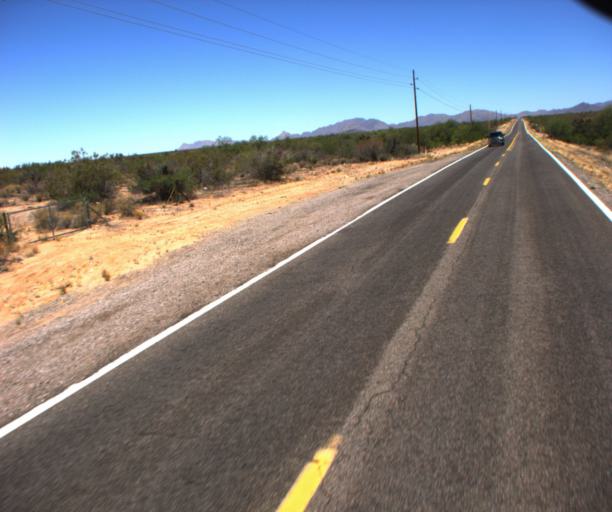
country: US
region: Arizona
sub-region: Yavapai County
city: Congress
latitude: 34.0677
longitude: -112.8207
